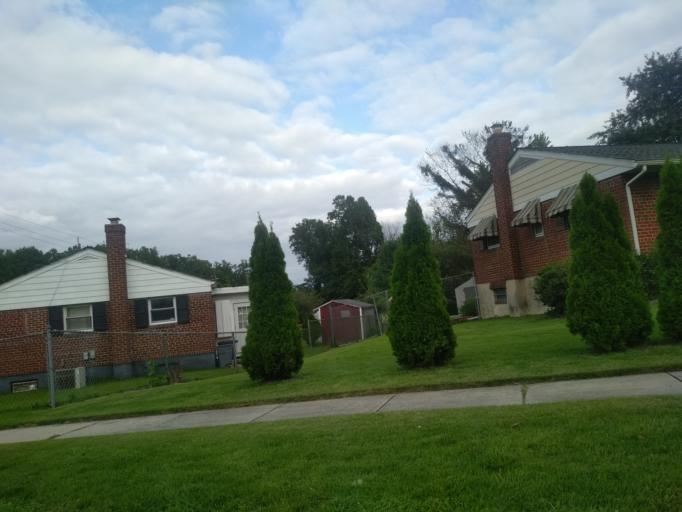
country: US
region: Maryland
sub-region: Montgomery County
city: North Bethesda
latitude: 39.0535
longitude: -77.0942
